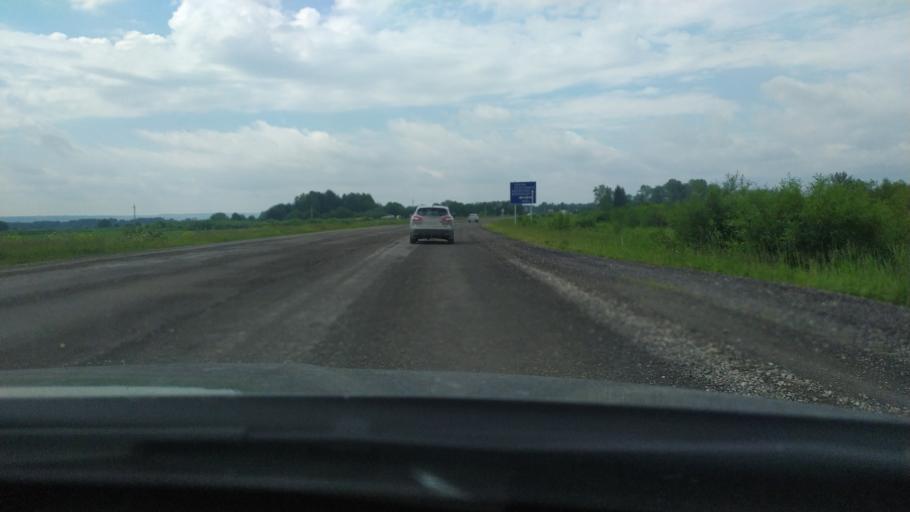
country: RU
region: Perm
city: Kalino
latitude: 58.2905
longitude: 57.4650
